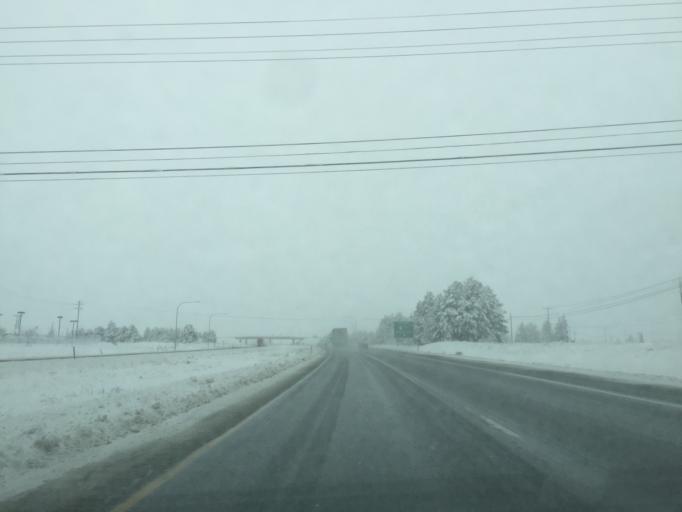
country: US
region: Washington
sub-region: Spokane County
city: Airway Heights
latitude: 47.5955
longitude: -117.5593
